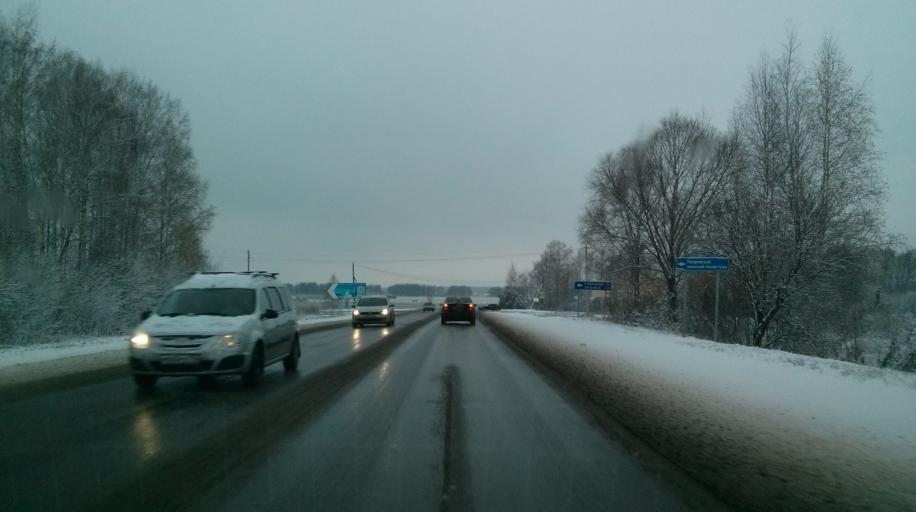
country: RU
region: Nizjnij Novgorod
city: Bogorodsk
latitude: 56.0871
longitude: 43.5312
